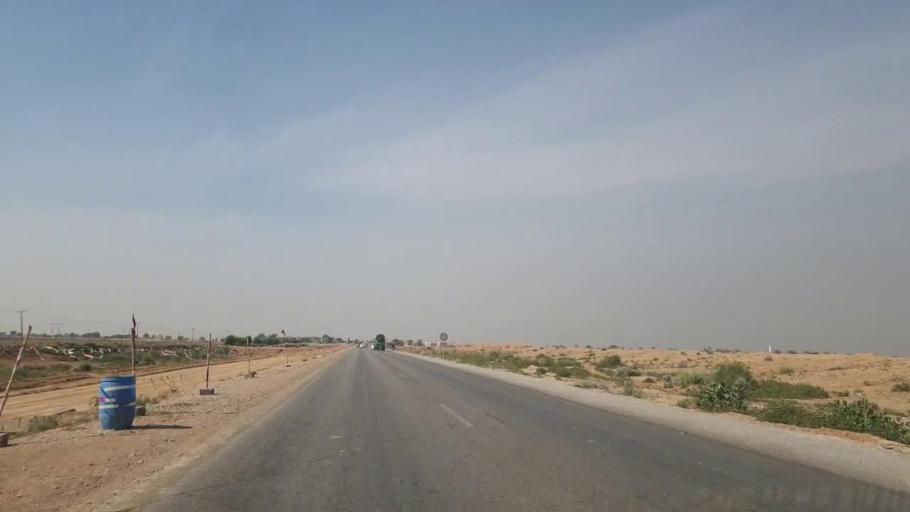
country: PK
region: Sindh
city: Sann
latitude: 26.0236
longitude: 68.1313
